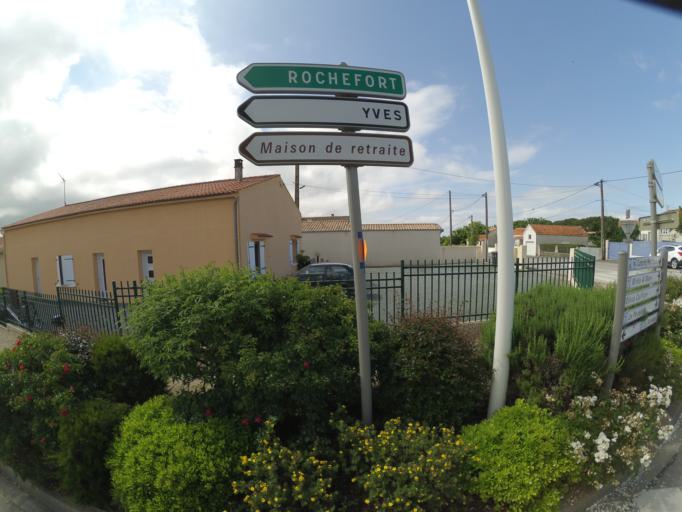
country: FR
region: Poitou-Charentes
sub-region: Departement de la Charente-Maritime
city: Chatelaillon-Plage
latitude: 46.0585
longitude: -1.0866
